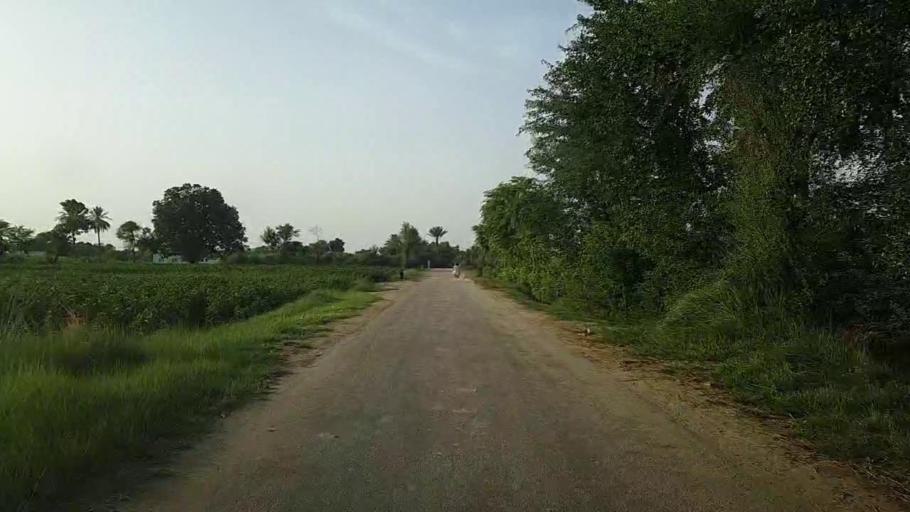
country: PK
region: Sindh
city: Bhiria
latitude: 26.9075
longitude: 68.2638
